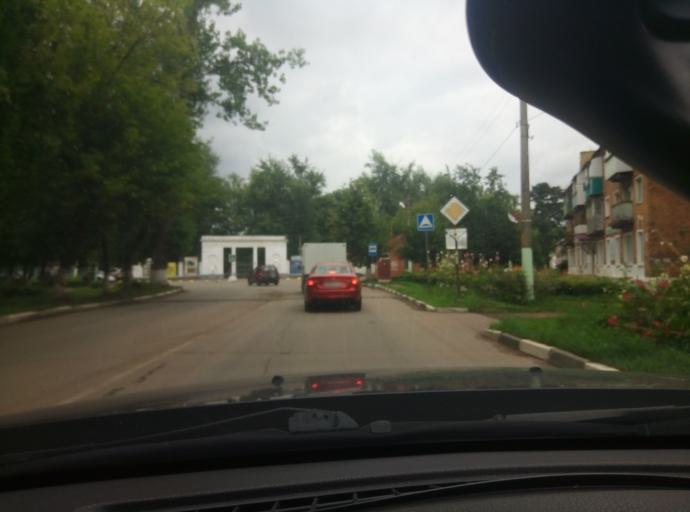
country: RU
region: Tula
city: Kimovsk
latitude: 53.9704
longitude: 38.5348
